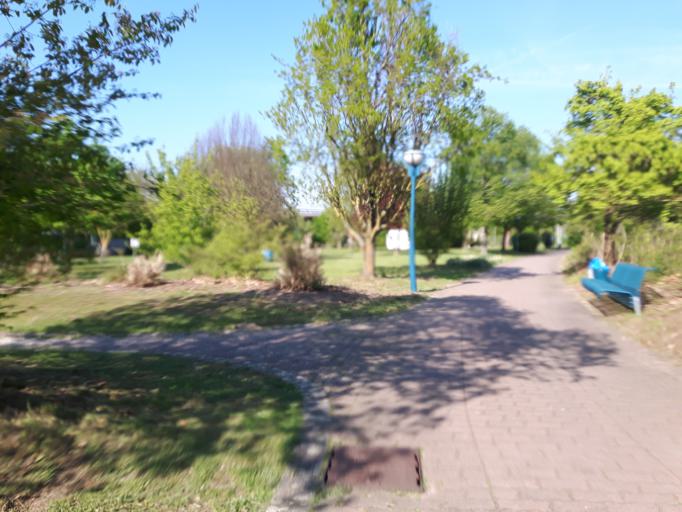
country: DE
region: Baden-Wuerttemberg
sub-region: Karlsruhe Region
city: Hockenheim
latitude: 49.3313
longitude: 8.5467
